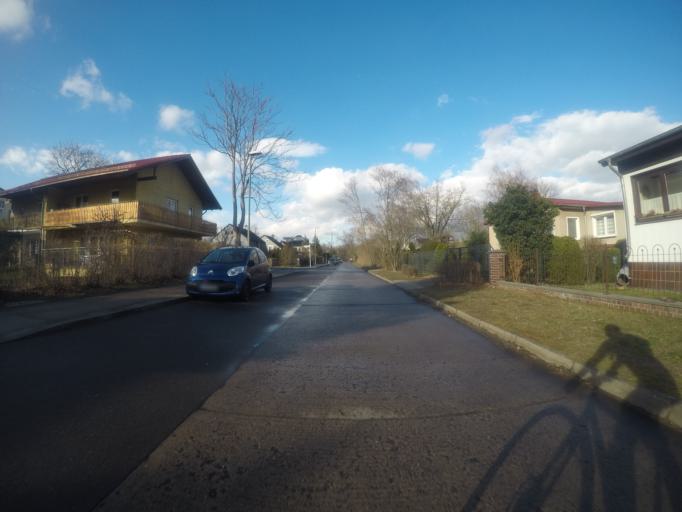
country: DE
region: Berlin
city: Karlshorst
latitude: 52.4942
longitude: 13.5399
